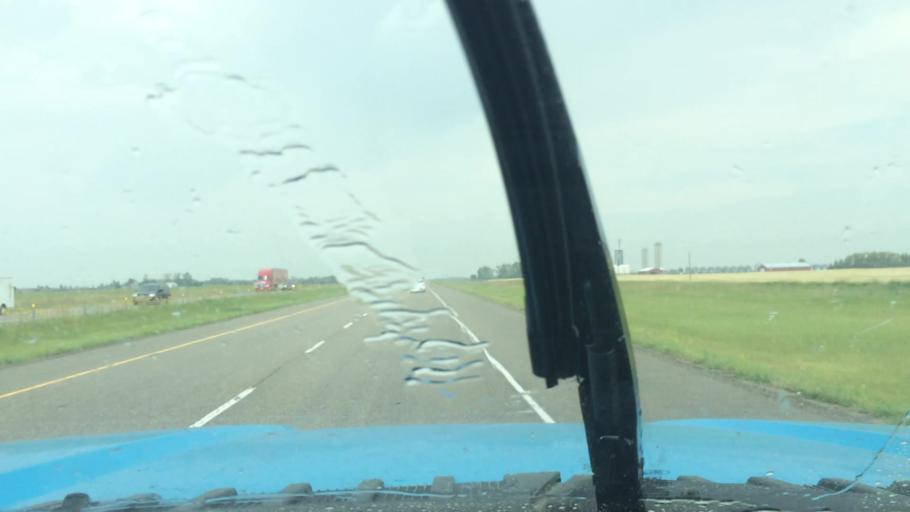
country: CA
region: Alberta
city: Olds
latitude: 51.7131
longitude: -114.0253
